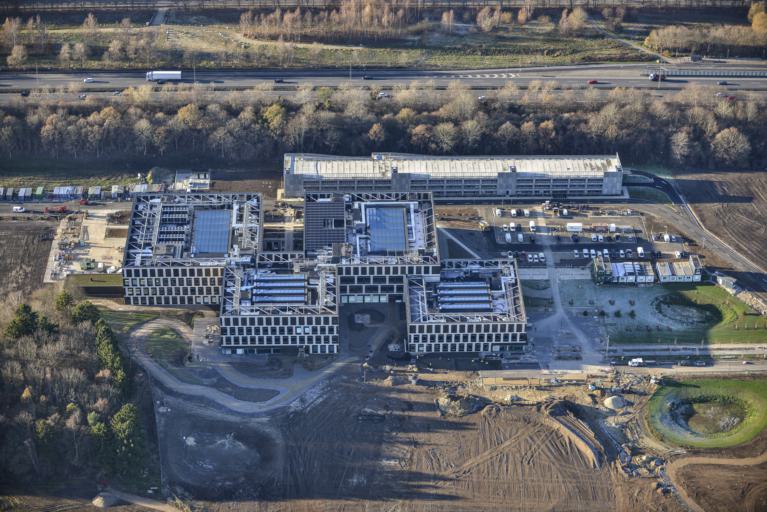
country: DK
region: Capital Region
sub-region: Lyngby-Tarbaek Kommune
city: Kongens Lyngby
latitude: 55.7859
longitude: 12.5313
